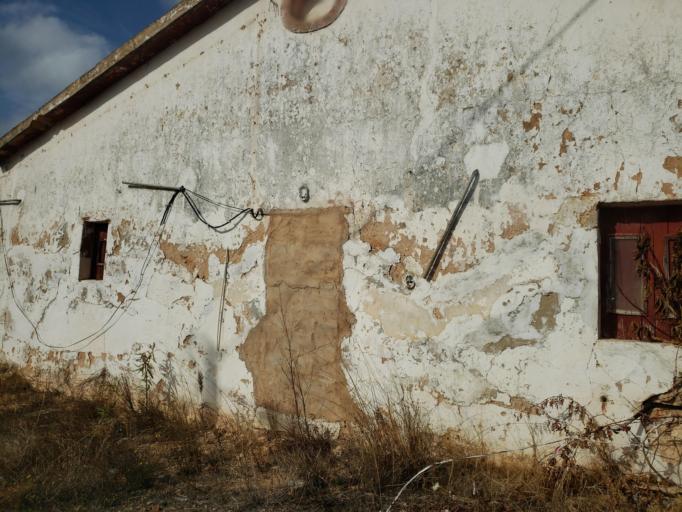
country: PT
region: Faro
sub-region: Portimao
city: Alvor
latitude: 37.1668
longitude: -8.5778
